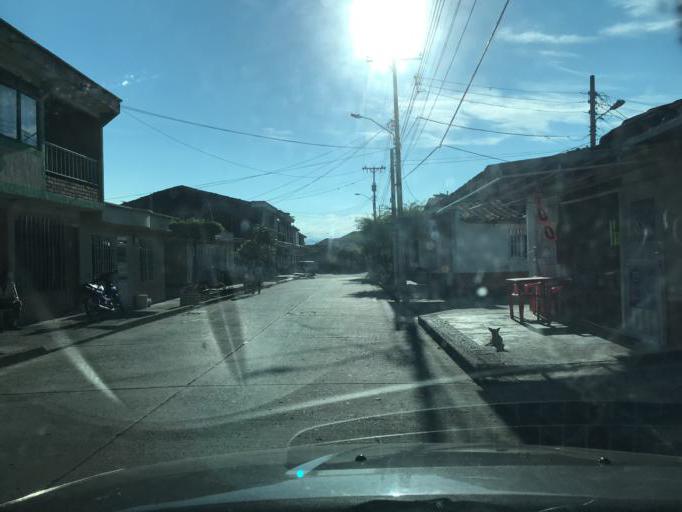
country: CO
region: Valle del Cauca
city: Cartago
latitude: 4.7627
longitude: -75.9335
